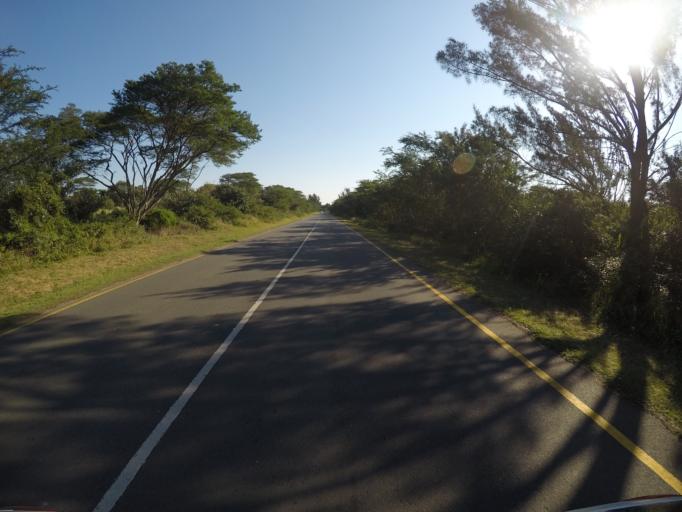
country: ZA
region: KwaZulu-Natal
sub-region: uThungulu District Municipality
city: Richards Bay
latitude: -28.7818
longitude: 32.0716
